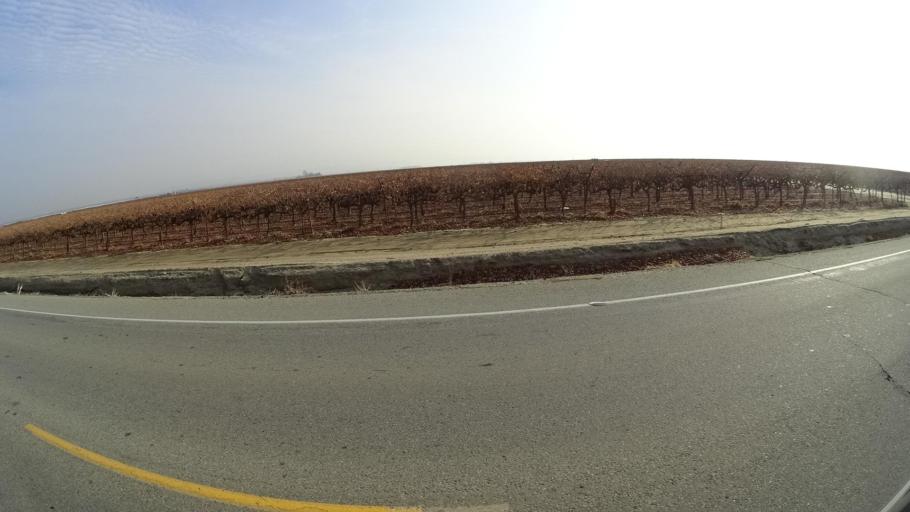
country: US
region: California
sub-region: Kern County
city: Arvin
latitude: 35.0768
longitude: -118.9174
